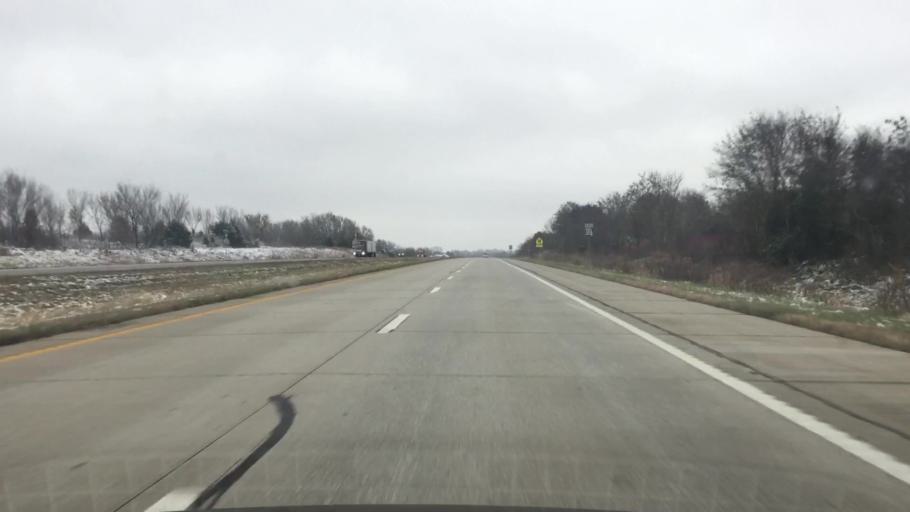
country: US
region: Missouri
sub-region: Saint Clair County
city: Osceola
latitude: 38.2050
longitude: -93.7523
